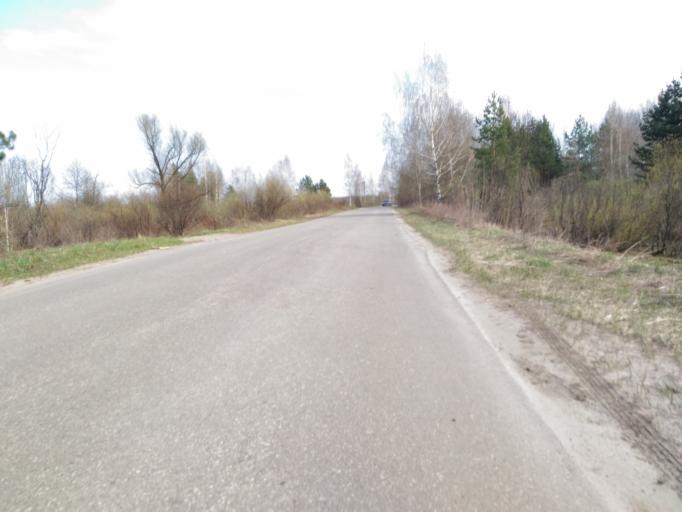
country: RU
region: Vladimir
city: Petushki
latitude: 55.9096
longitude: 39.4685
